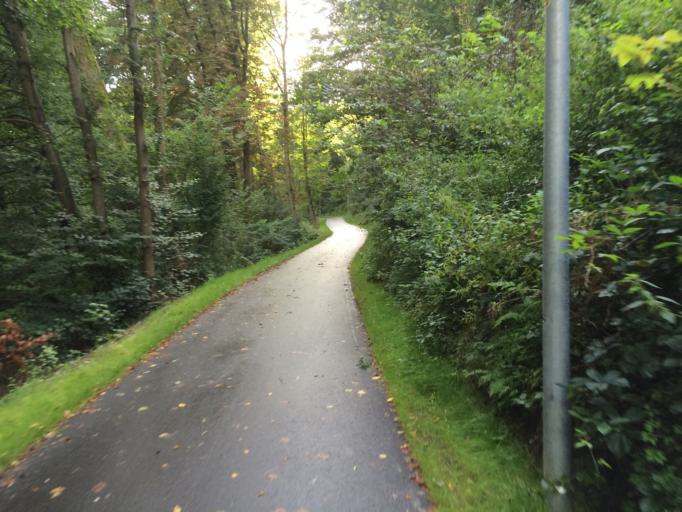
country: DE
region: North Rhine-Westphalia
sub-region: Regierungsbezirk Detmold
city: Detmold
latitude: 51.9263
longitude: 8.8676
